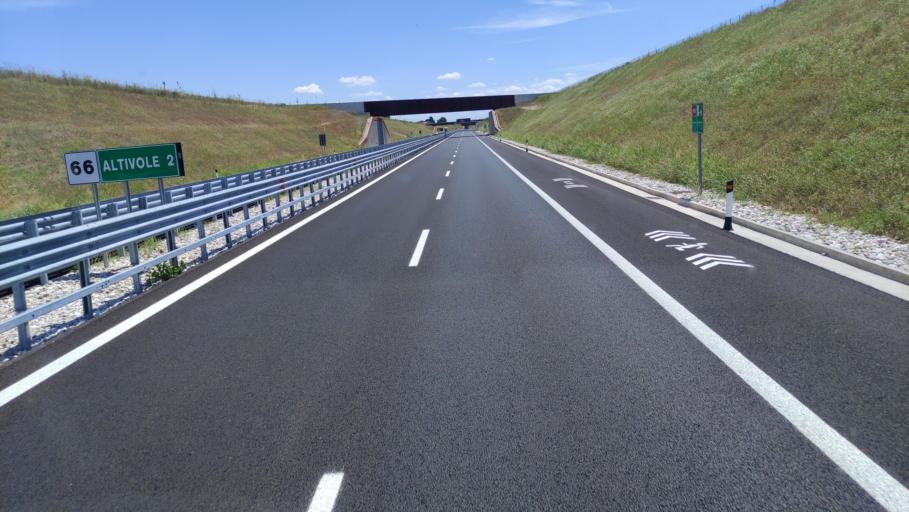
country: IT
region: Veneto
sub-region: Provincia di Treviso
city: Altivole
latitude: 45.7417
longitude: 11.9378
